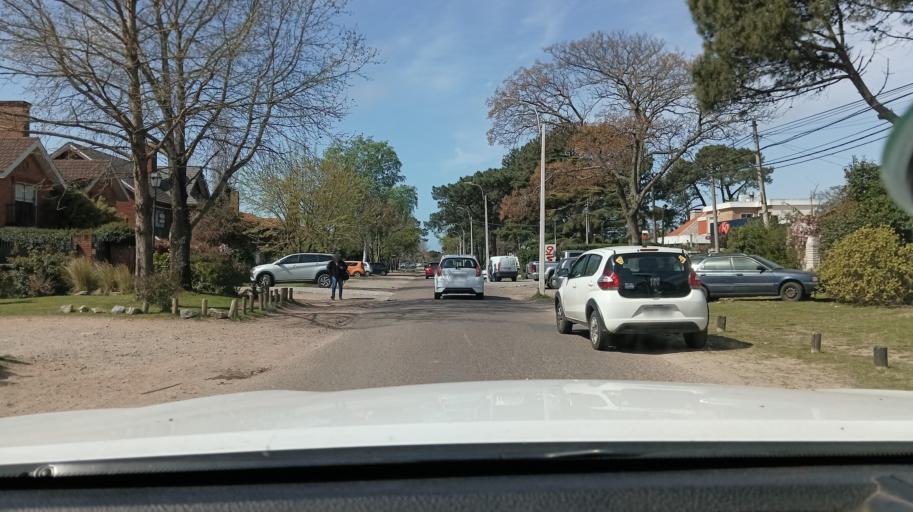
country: UY
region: Canelones
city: Barra de Carrasco
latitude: -34.8748
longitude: -56.0439
